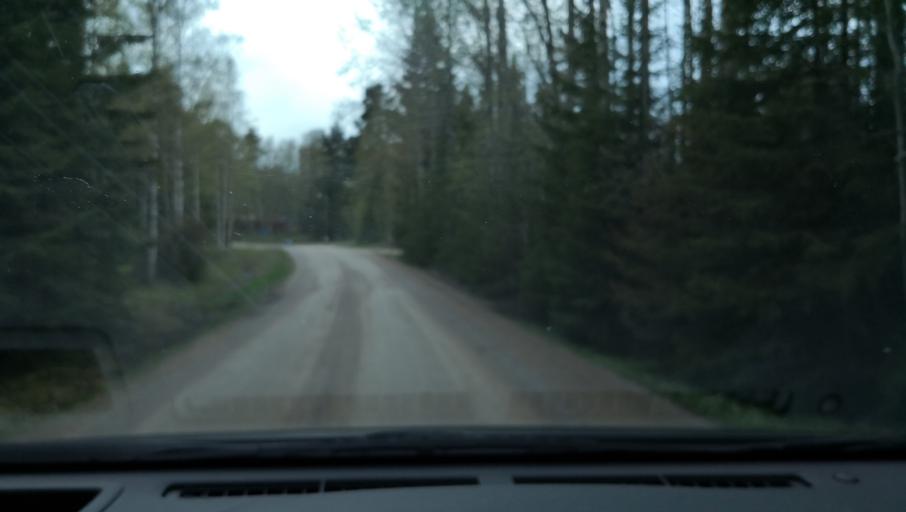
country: SE
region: Vaestmanland
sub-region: Fagersta Kommun
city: Fagersta
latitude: 60.1184
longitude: 15.7946
